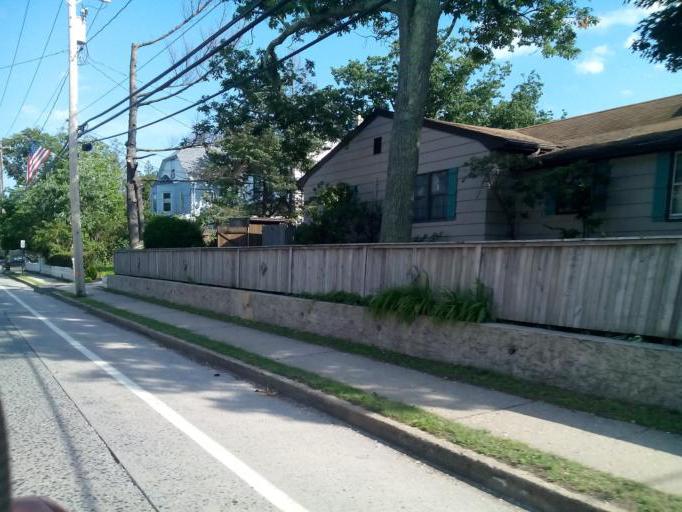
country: US
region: New York
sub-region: Nassau County
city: Bayville
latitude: 40.9082
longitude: -73.5548
